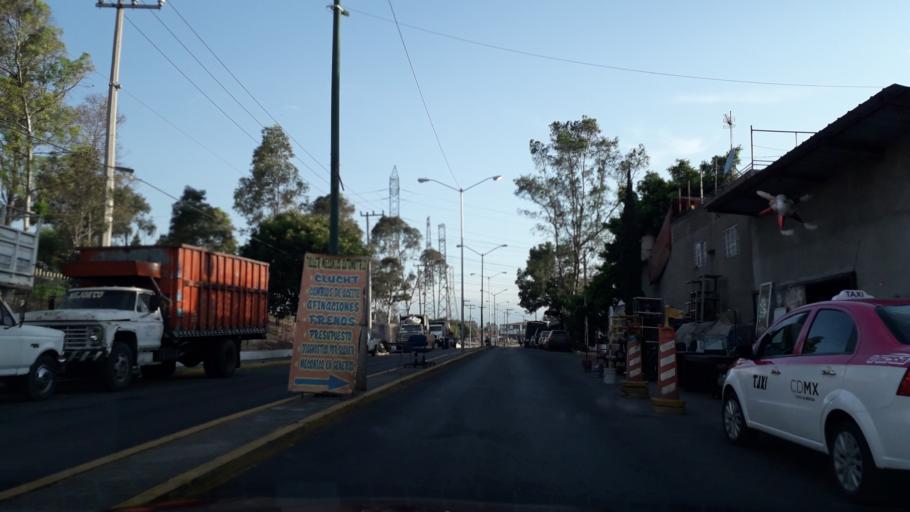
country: MX
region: Mexico City
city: Iztapalapa
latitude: 19.3652
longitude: -99.0479
